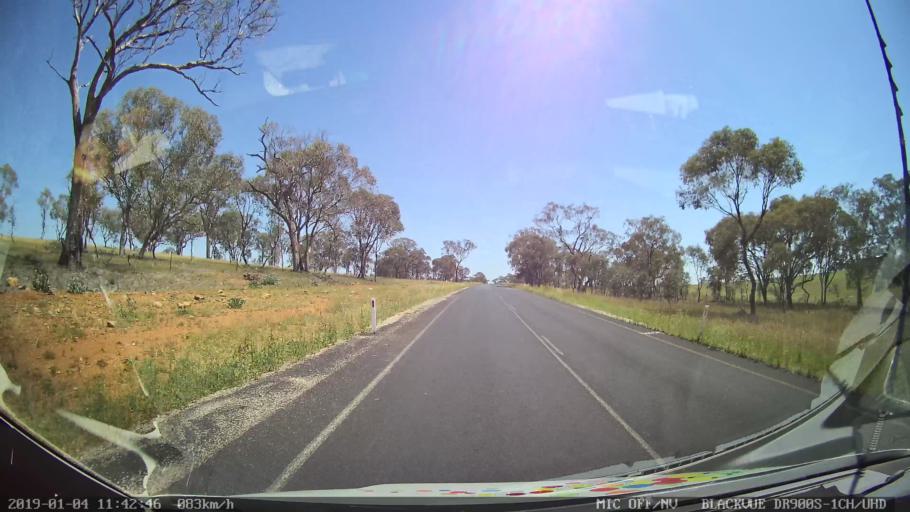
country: AU
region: New South Wales
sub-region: Cabonne
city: Molong
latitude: -32.9775
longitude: 148.7856
